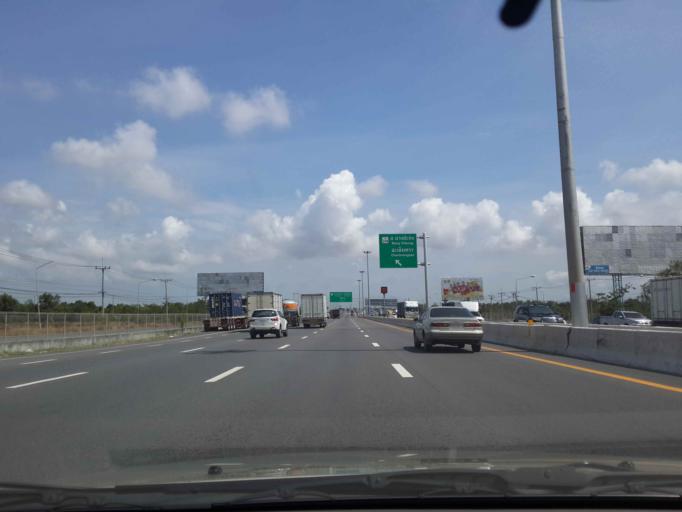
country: TH
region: Chachoengsao
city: Bang Pakong
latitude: 13.5435
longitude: 101.0052
